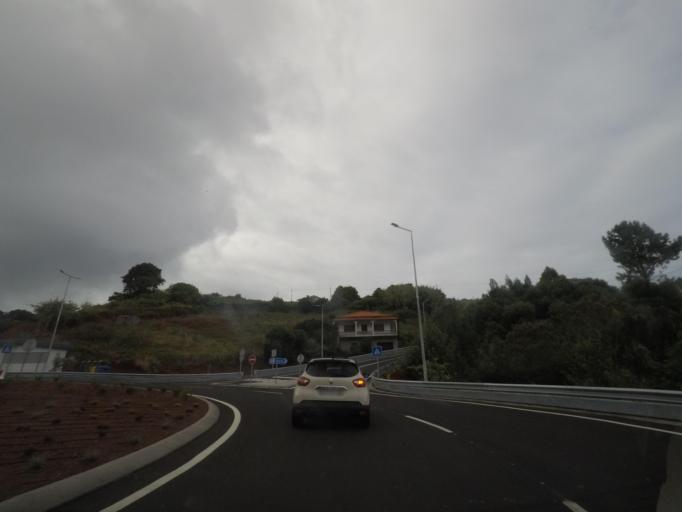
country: PT
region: Madeira
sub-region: Santana
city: Santana
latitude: 32.8304
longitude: -16.9078
